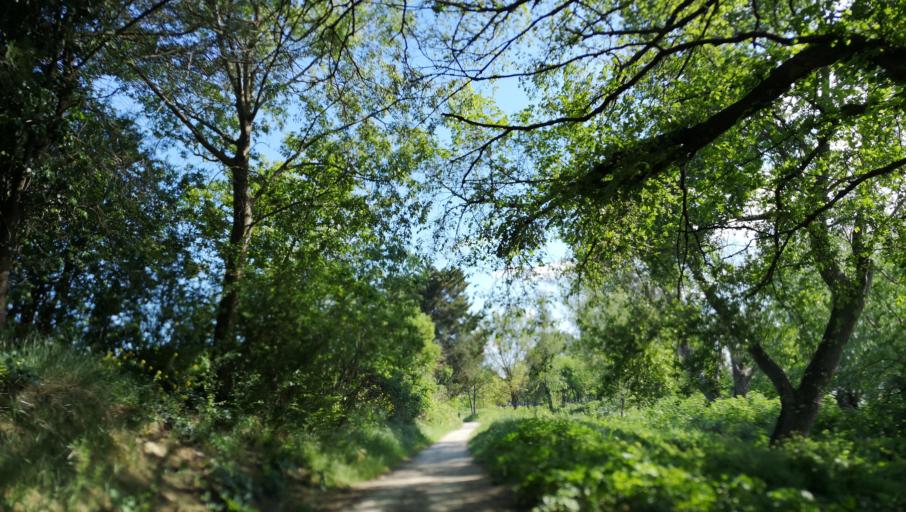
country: FR
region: Midi-Pyrenees
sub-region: Departement de la Haute-Garonne
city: Blagnac
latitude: 43.6351
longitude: 1.4048
